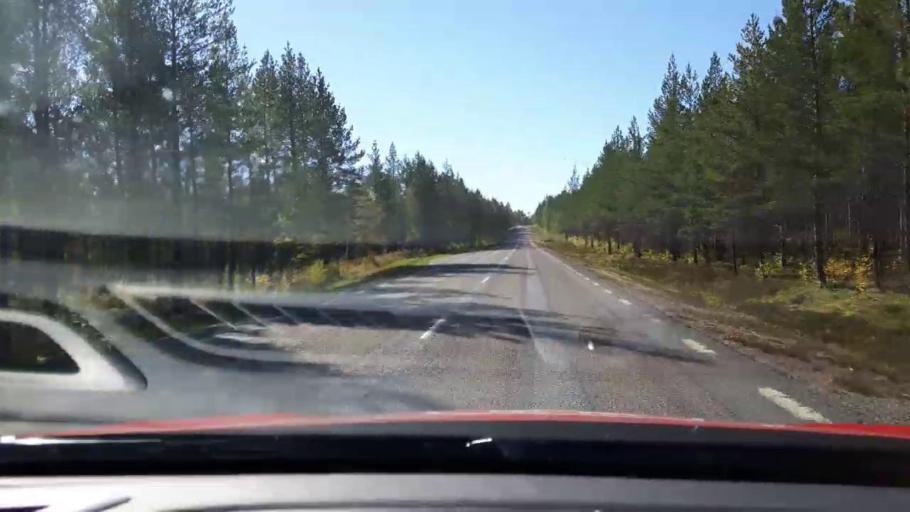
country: SE
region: Jaemtland
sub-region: Harjedalens Kommun
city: Sveg
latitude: 62.1342
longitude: 14.1688
